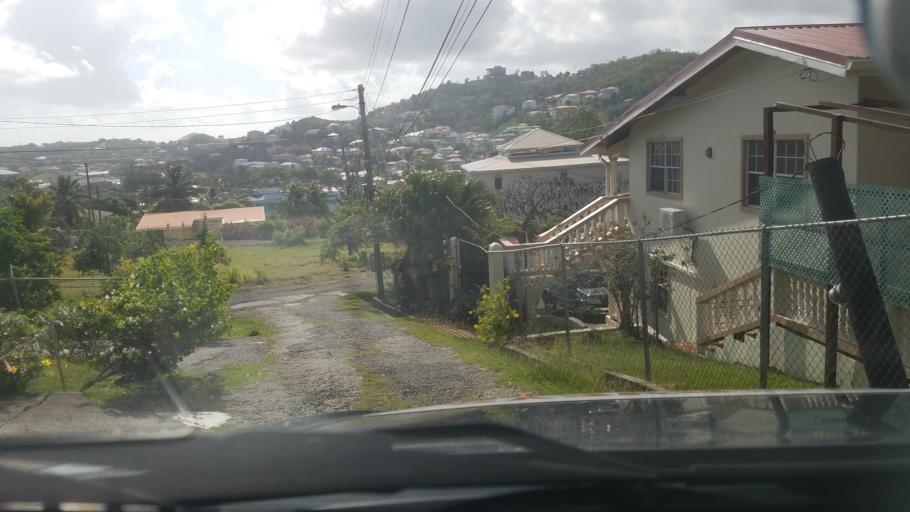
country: LC
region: Gros-Islet
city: Gros Islet
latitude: 14.0666
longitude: -60.9584
